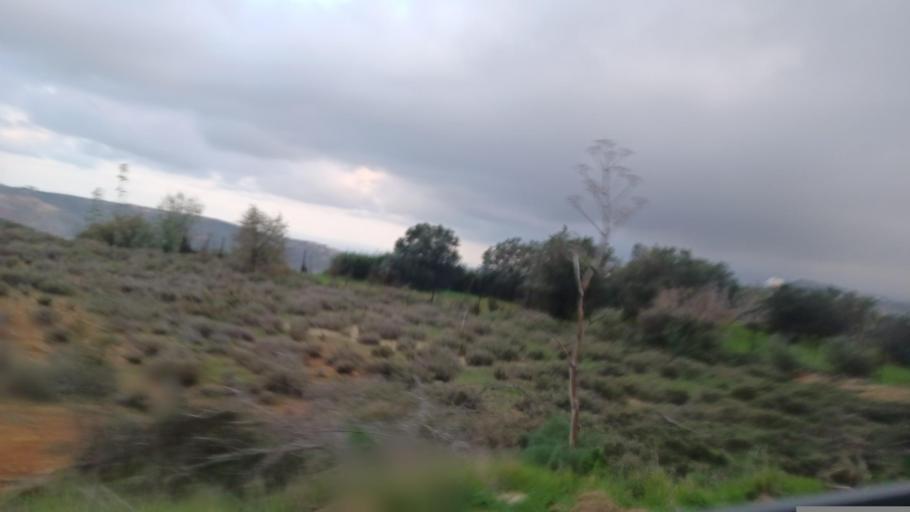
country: CY
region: Pafos
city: Mesogi
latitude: 34.7849
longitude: 32.4975
